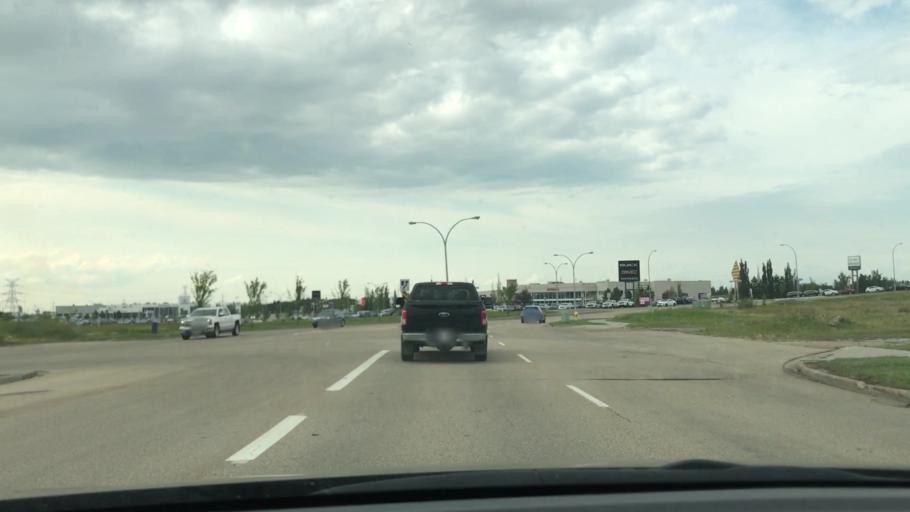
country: CA
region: Alberta
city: Sherwood Park
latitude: 53.5425
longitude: -113.3243
